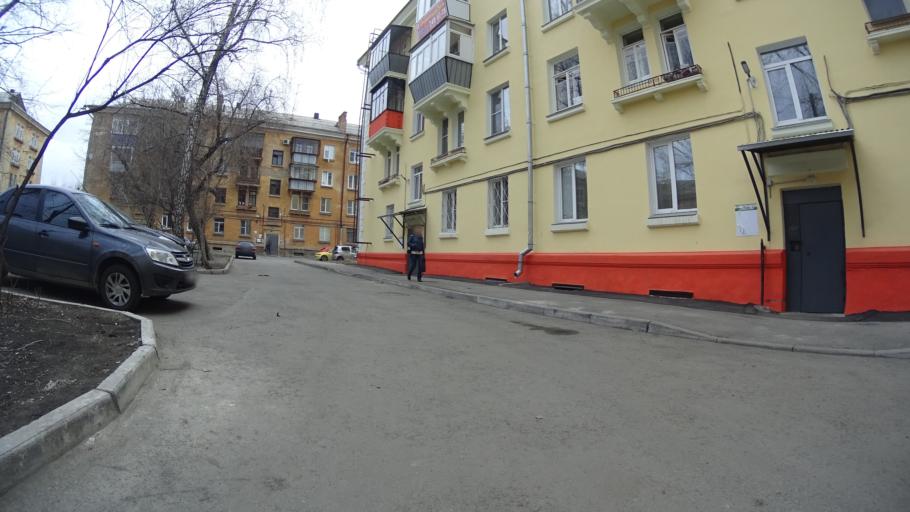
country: RU
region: Chelyabinsk
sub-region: Gorod Chelyabinsk
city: Chelyabinsk
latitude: 55.1637
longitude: 61.4404
